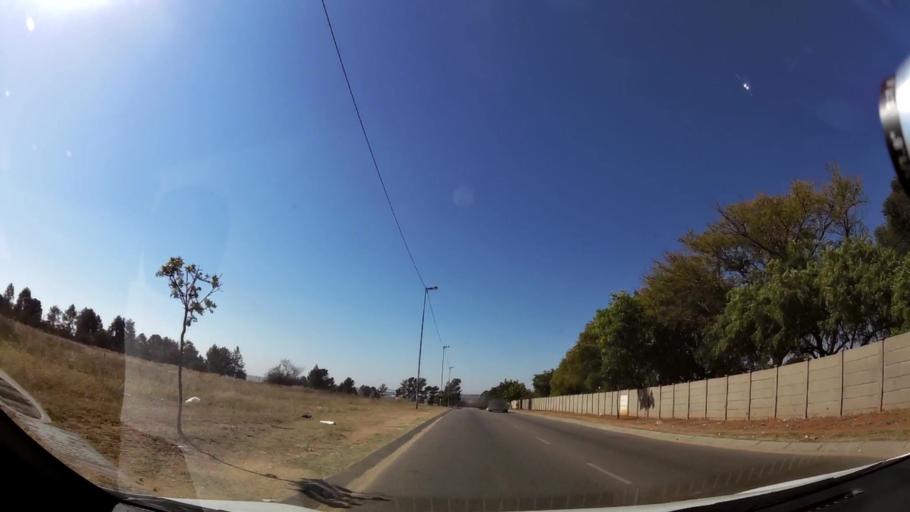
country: ZA
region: Gauteng
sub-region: City of Johannesburg Metropolitan Municipality
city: Midrand
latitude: -25.9424
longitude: 28.0976
